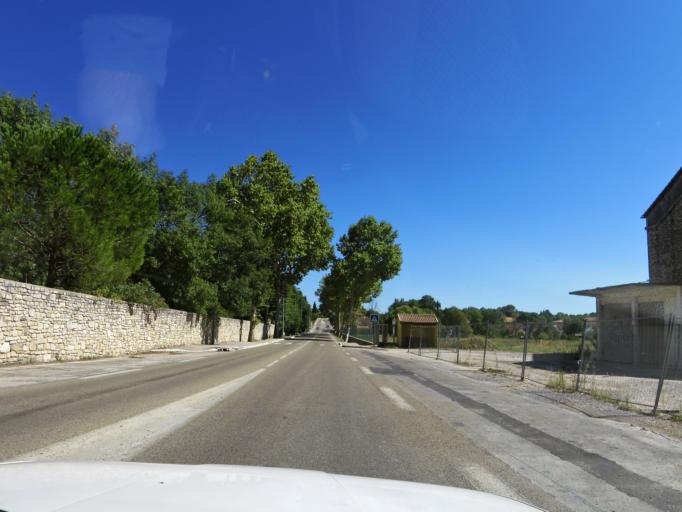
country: FR
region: Languedoc-Roussillon
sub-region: Departement du Gard
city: Vezenobres
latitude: 44.0495
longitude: 4.1409
